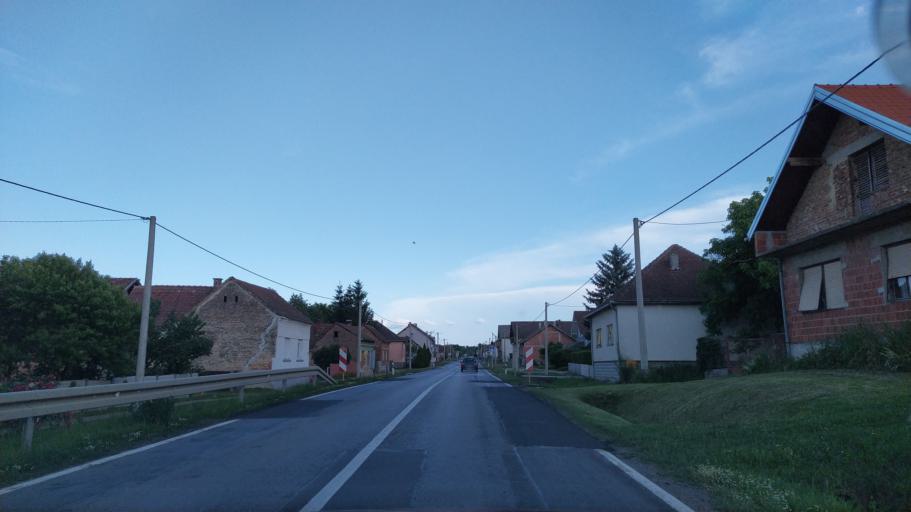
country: HR
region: Virovitick-Podravska
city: Slatina
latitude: 45.7318
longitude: 17.6246
